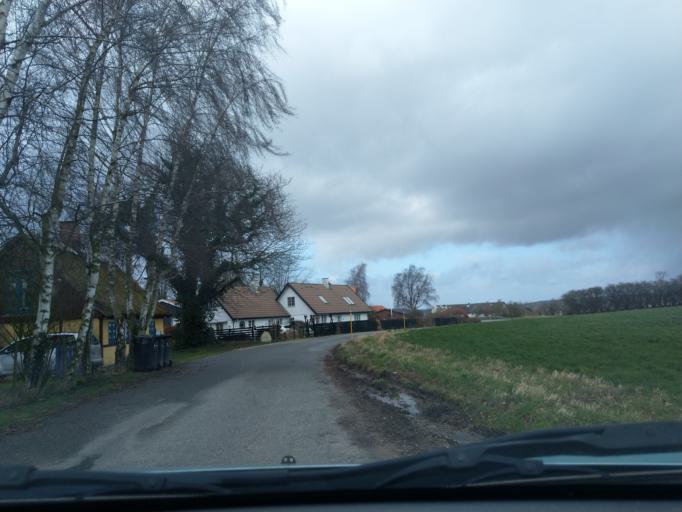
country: DK
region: Zealand
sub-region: Naestved Kommune
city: Fuglebjerg
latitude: 55.3514
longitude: 11.5806
